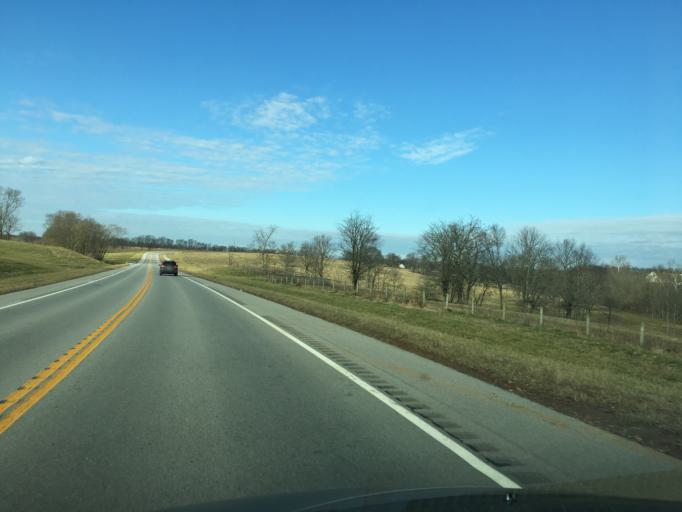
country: US
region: Kentucky
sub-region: Scott County
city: Georgetown
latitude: 38.2269
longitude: -84.5856
